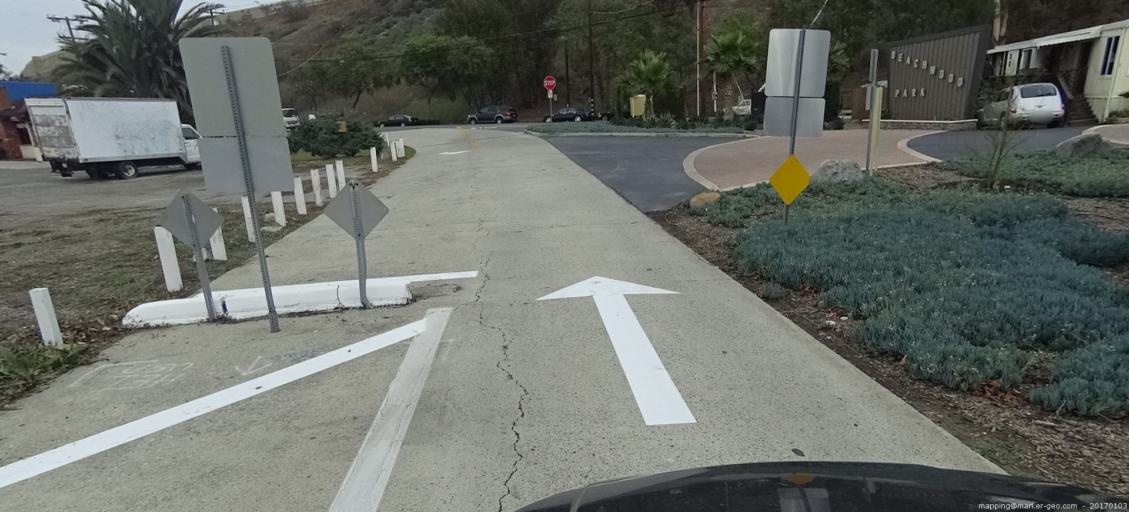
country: US
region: California
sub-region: Orange County
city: Dana Point
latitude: 33.4689
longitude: -117.6755
